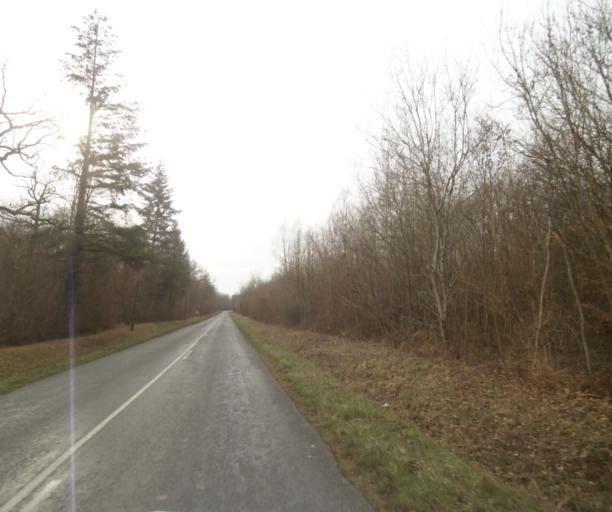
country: FR
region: Champagne-Ardenne
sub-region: Departement de la Haute-Marne
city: Villiers-en-Lieu
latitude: 48.6917
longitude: 4.8904
